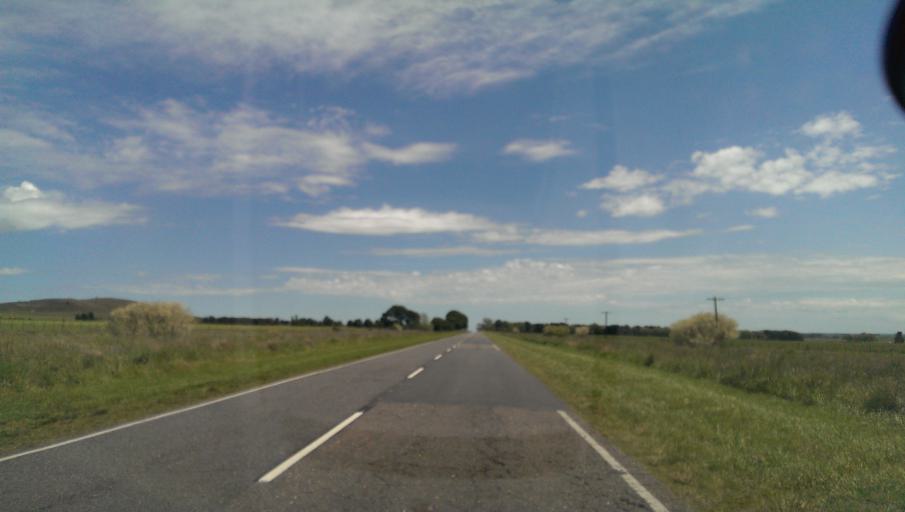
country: AR
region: Buenos Aires
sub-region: Partido de Tornquist
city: Tornquist
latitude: -38.0540
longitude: -62.1734
